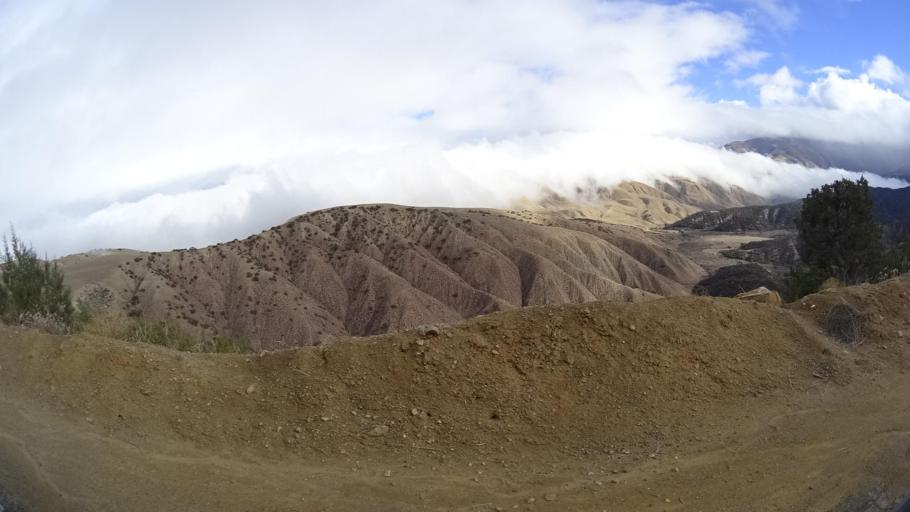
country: US
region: California
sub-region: Kern County
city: Maricopa
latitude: 34.8925
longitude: -119.3585
